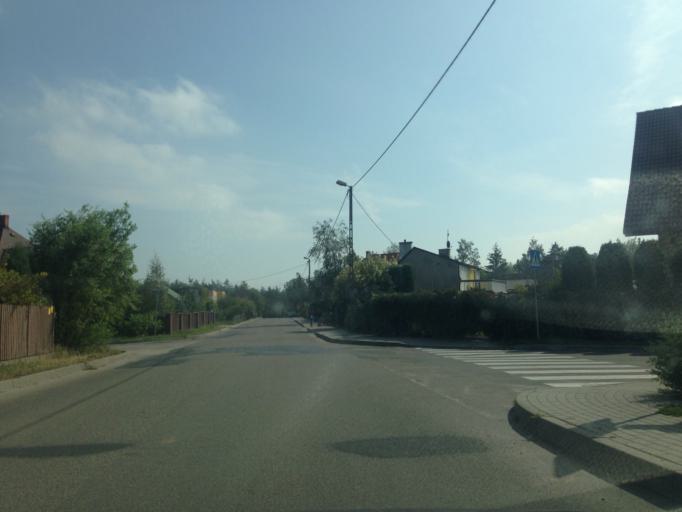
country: PL
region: Kujawsko-Pomorskie
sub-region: Powiat brodnicki
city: Brodnica
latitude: 53.2729
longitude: 19.4163
